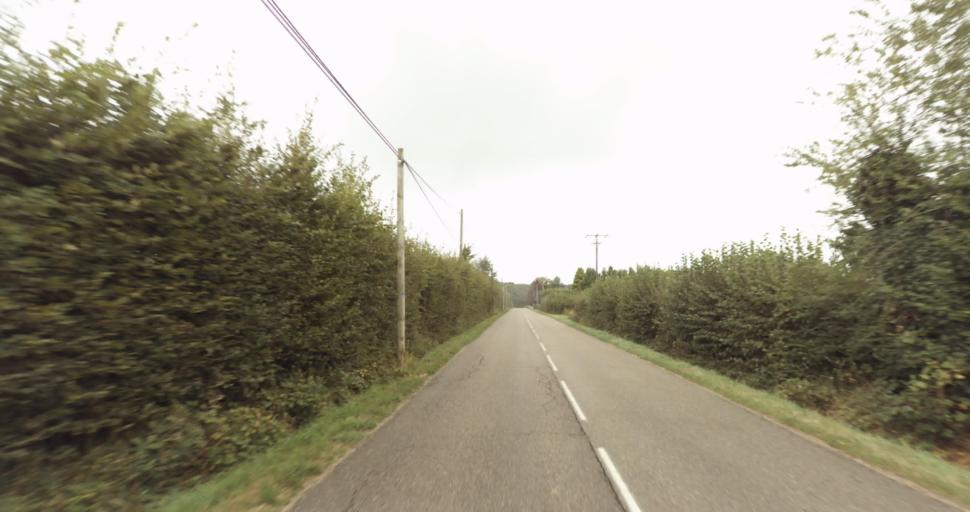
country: FR
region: Lower Normandy
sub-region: Departement de l'Orne
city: Vimoutiers
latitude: 48.8898
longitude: 0.1973
